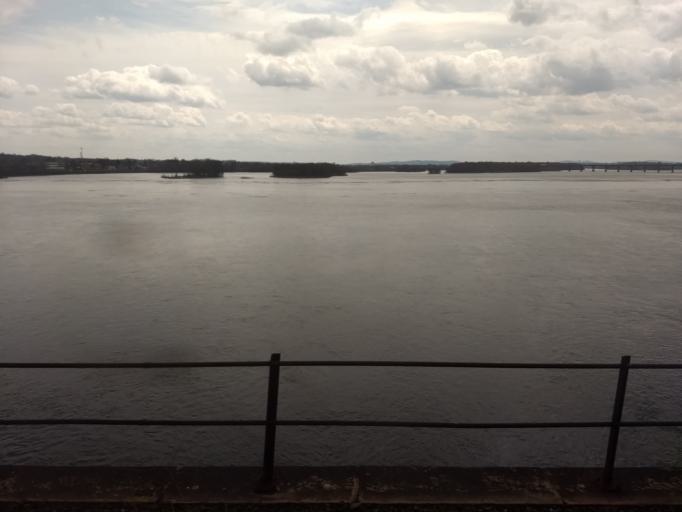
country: US
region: Pennsylvania
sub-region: Perry County
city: Marysville
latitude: 40.3338
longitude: -76.9088
